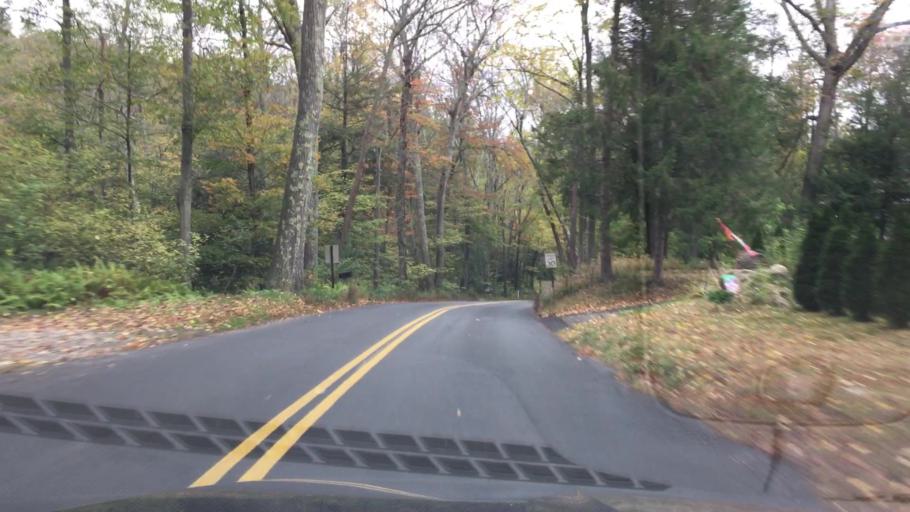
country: US
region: Connecticut
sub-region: Tolland County
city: Somers
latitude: 41.9727
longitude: -72.4162
